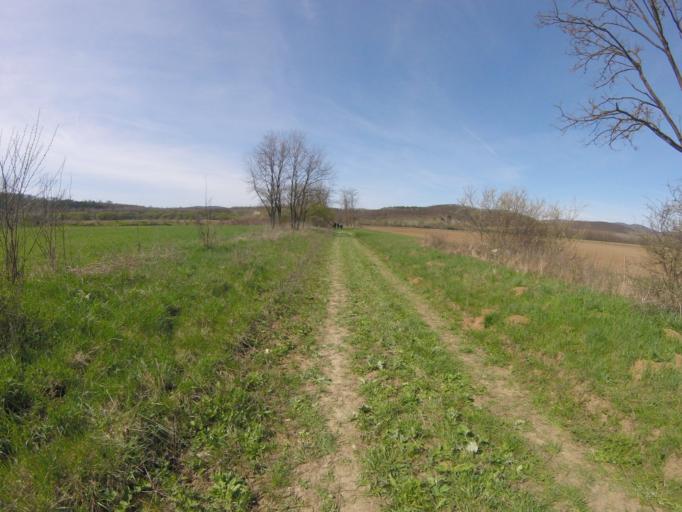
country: HU
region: Borsod-Abauj-Zemplen
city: Szendro
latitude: 48.4182
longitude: 20.7634
